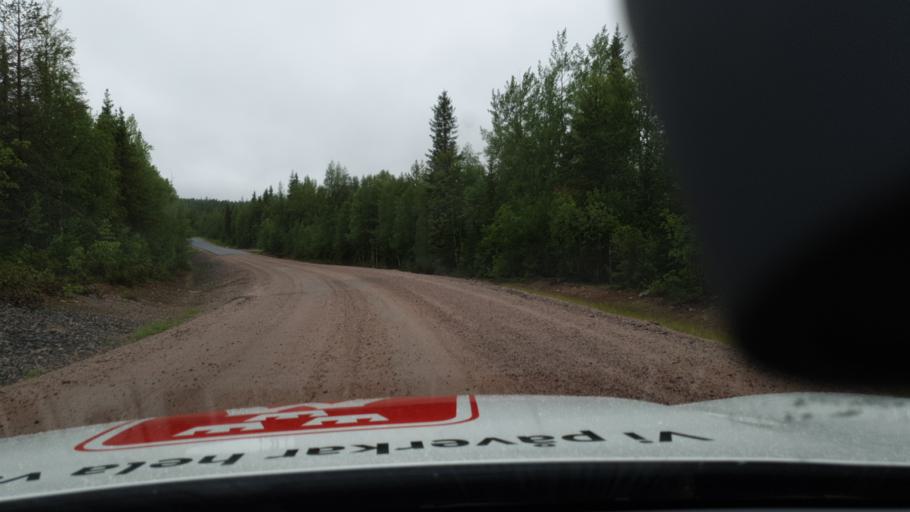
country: SE
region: Norrbotten
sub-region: Overtornea Kommun
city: OEvertornea
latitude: 66.5116
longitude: 23.4026
